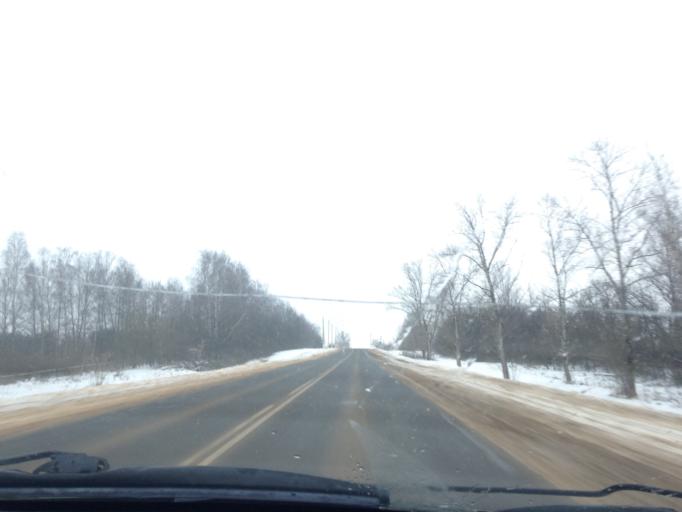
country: RU
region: Tula
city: Shchekino
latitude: 53.9682
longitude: 37.4969
